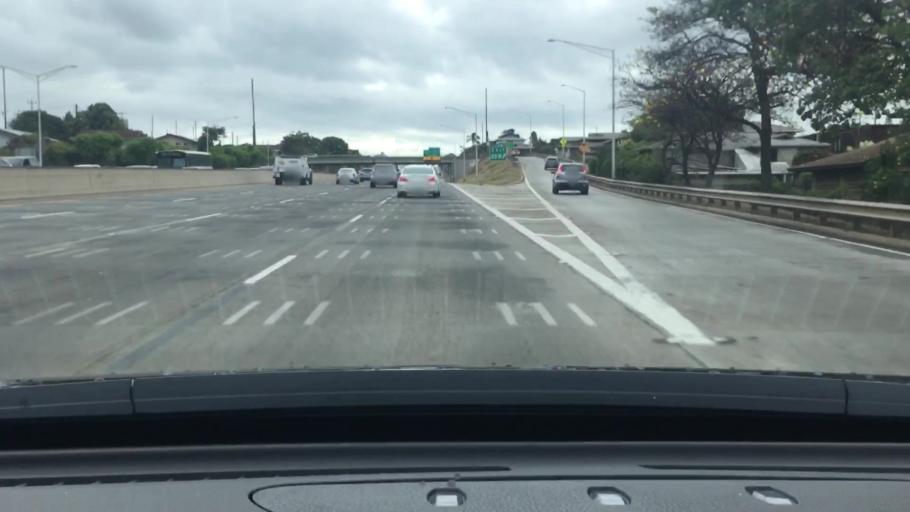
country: US
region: Hawaii
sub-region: Honolulu County
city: Honolulu
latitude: 21.2847
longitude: -157.8092
